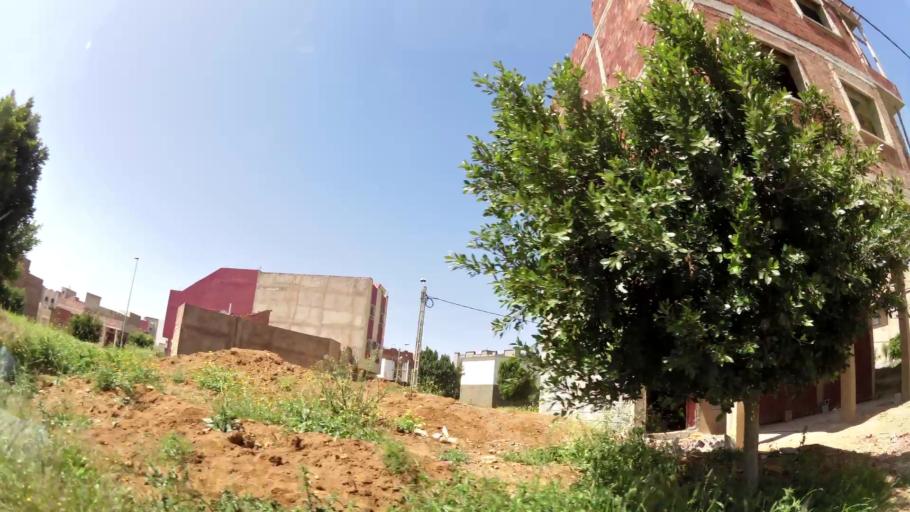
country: MA
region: Rabat-Sale-Zemmour-Zaer
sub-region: Khemisset
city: Khemisset
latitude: 33.8103
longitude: -6.0867
